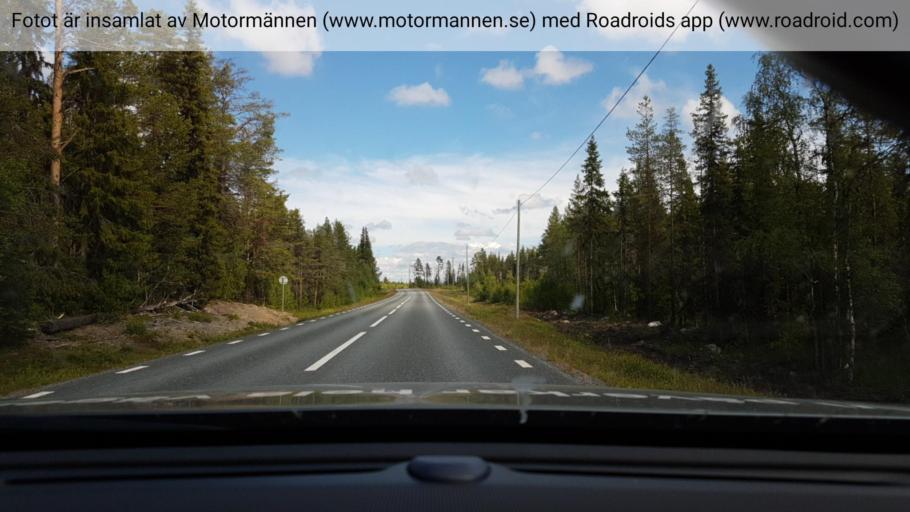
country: SE
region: Vaesterbotten
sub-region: Sorsele Kommun
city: Sorsele
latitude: 65.5565
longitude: 17.8631
